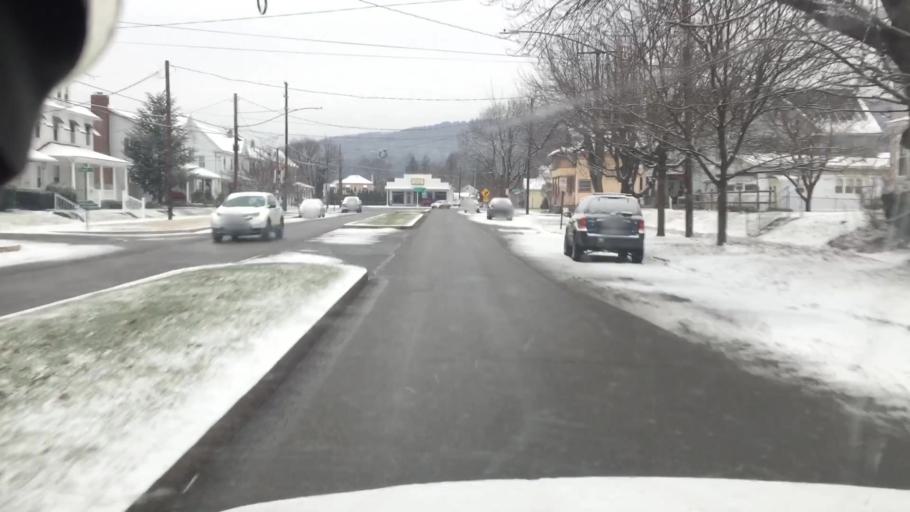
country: US
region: Pennsylvania
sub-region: Columbia County
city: Berwick
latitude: 41.0644
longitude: -76.2417
